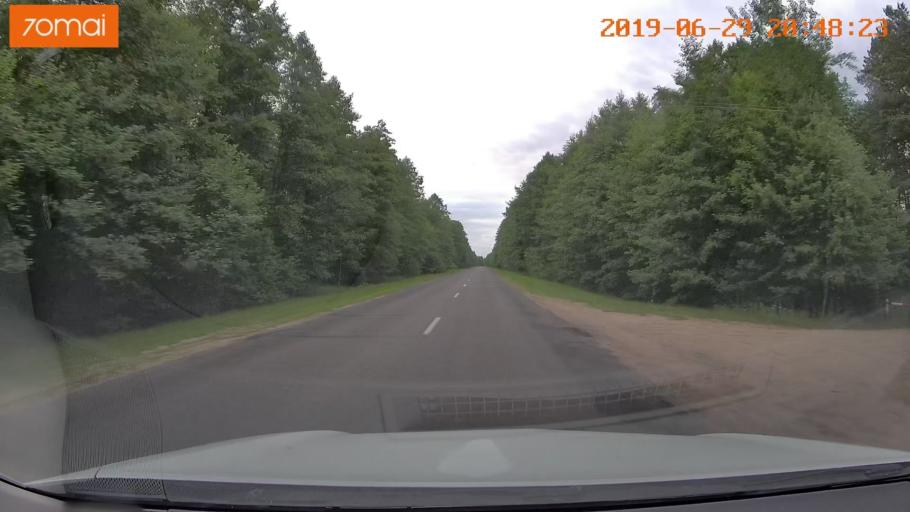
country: BY
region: Brest
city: Hantsavichy
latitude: 52.6500
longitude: 26.3176
